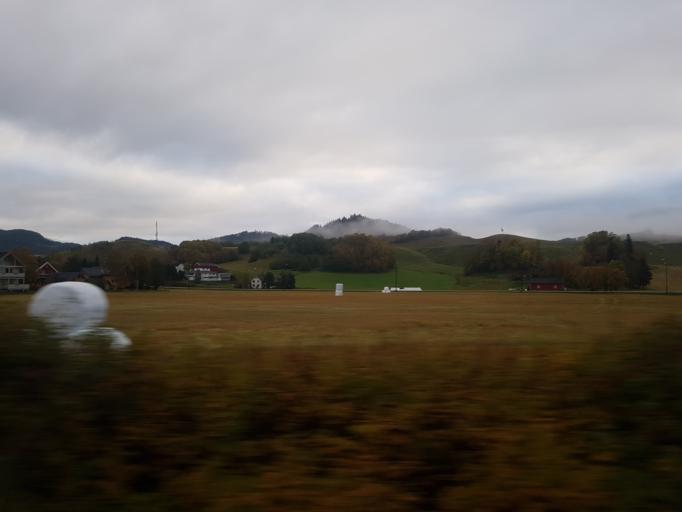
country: NO
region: Sor-Trondelag
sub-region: Melhus
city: Lundamo
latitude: 63.1872
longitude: 10.3099
